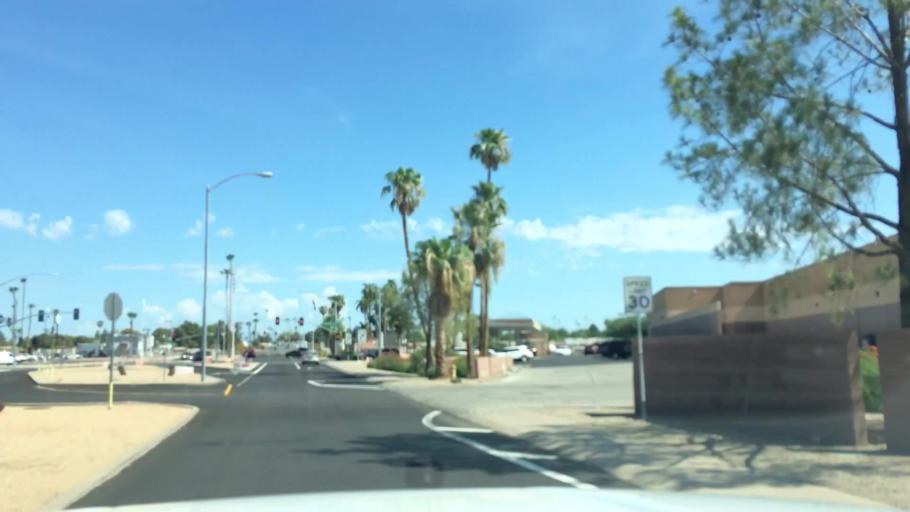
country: US
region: Arizona
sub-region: Maricopa County
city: Youngtown
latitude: 33.6002
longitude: -112.2898
